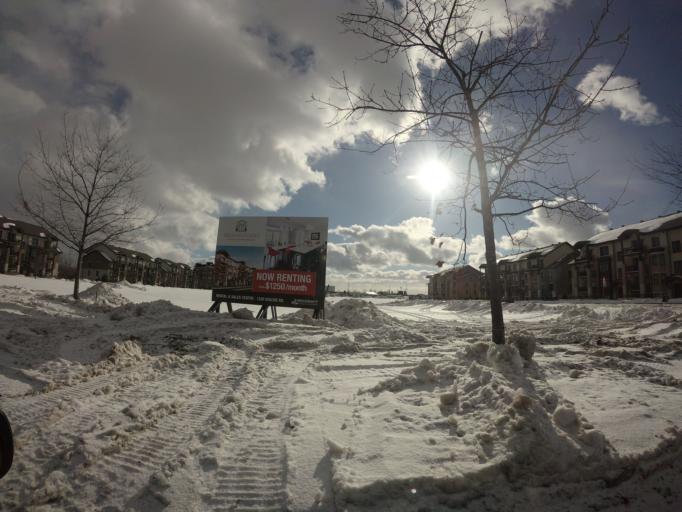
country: CA
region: Ontario
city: Ottawa
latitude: 45.4257
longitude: -75.6280
